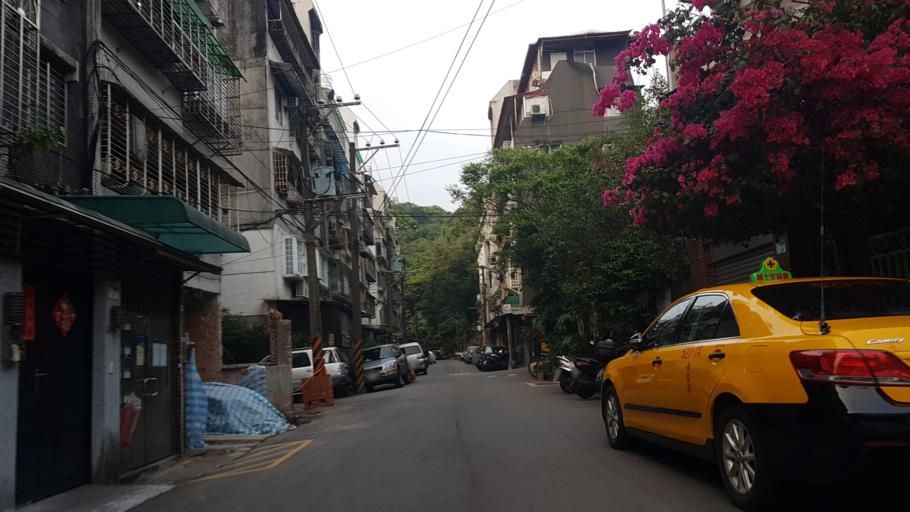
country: TW
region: Taipei
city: Taipei
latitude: 25.0042
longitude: 121.5515
